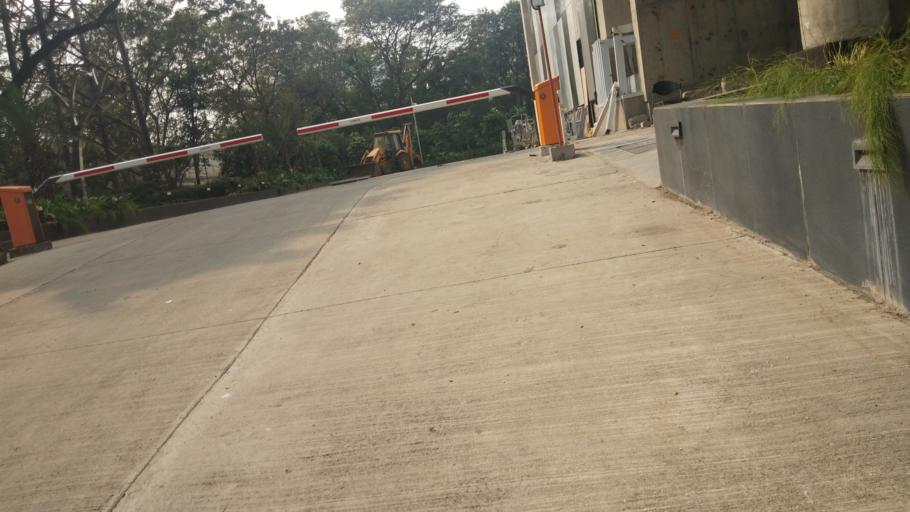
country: IN
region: Maharashtra
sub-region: Mumbai Suburban
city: Powai
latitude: 19.1515
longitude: 72.8547
